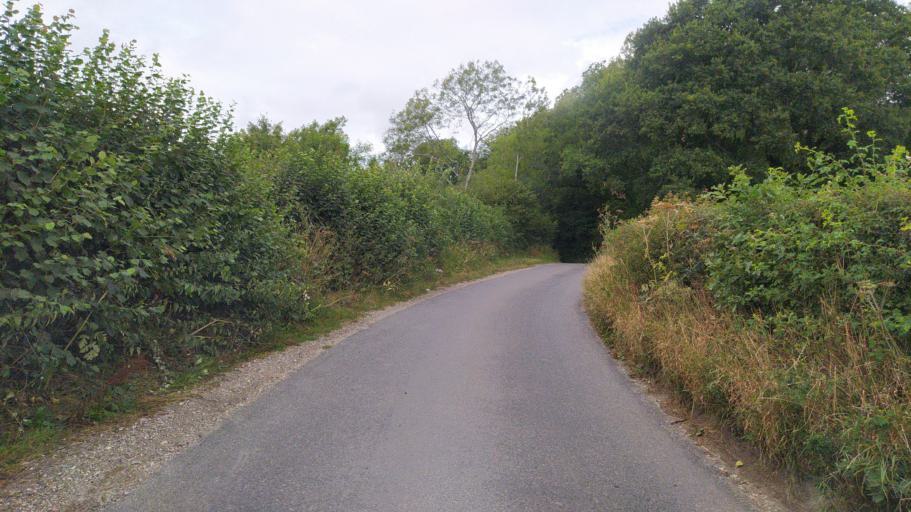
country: GB
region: England
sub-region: Hampshire
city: Petersfield
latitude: 50.9874
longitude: -0.9713
